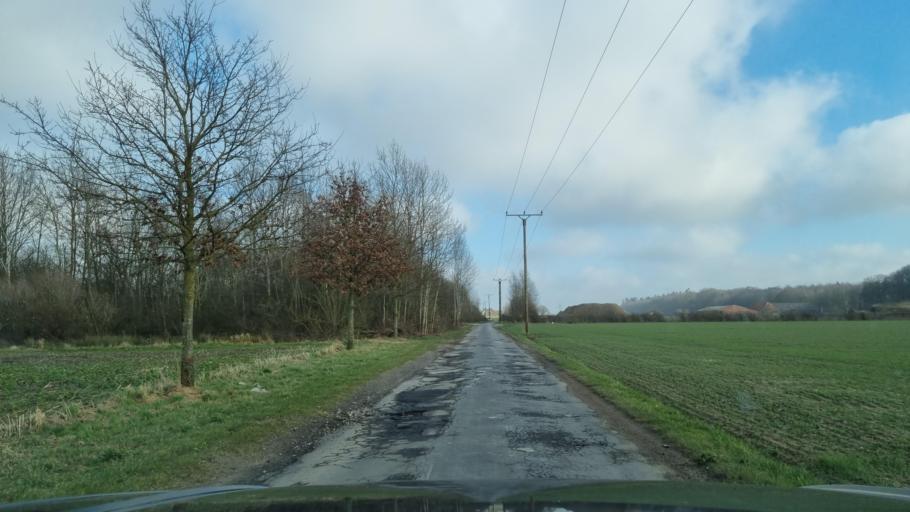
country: DE
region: North Rhine-Westphalia
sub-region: Regierungsbezirk Dusseldorf
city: Kleve
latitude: 51.7435
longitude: 6.1755
